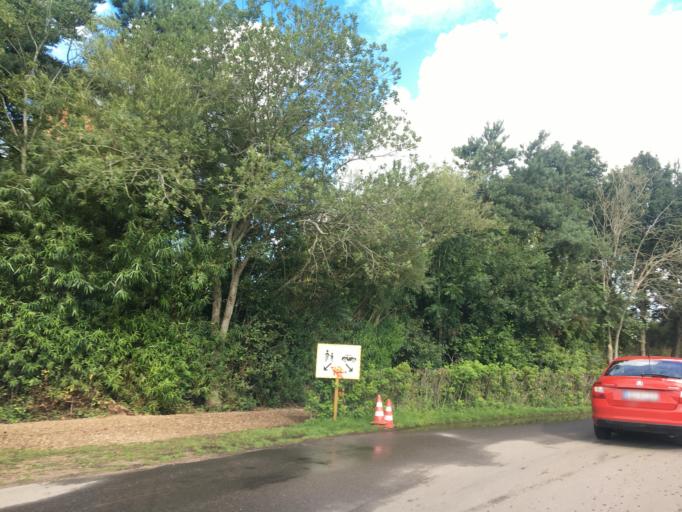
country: DK
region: Zealand
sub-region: Odsherred Kommune
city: Hojby
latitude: 55.8953
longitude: 11.6104
